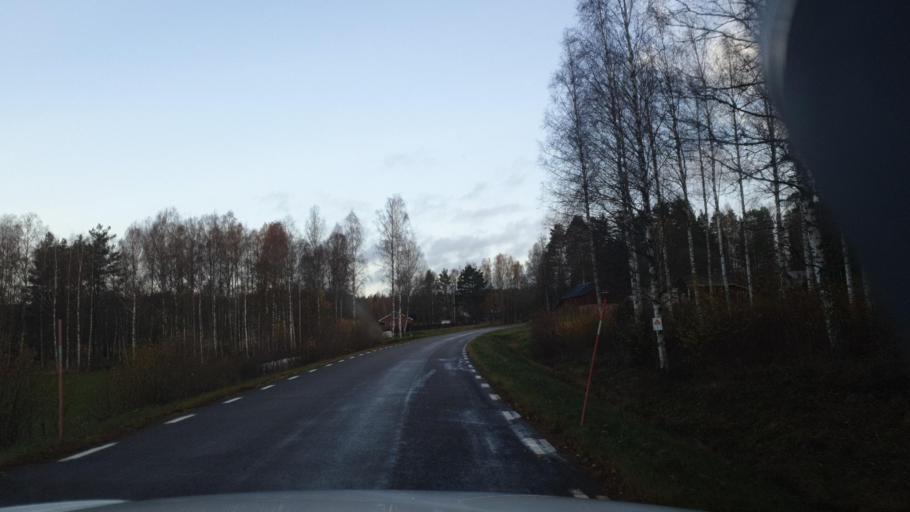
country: SE
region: Vaermland
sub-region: Arvika Kommun
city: Arvika
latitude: 59.5511
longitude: 12.7406
